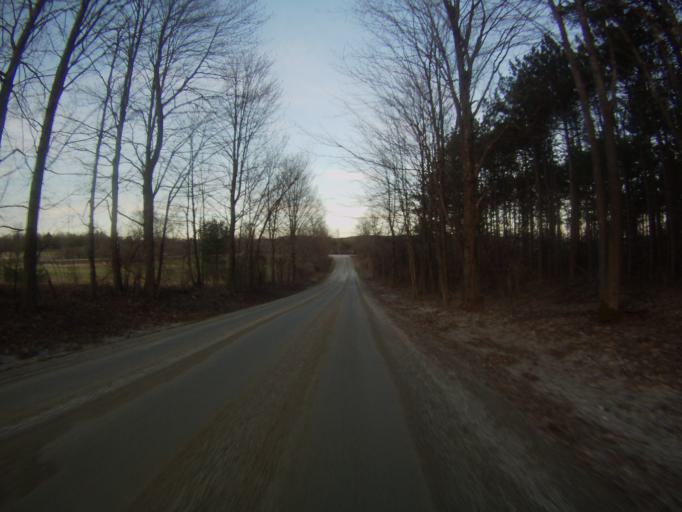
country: US
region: Vermont
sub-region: Addison County
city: Middlebury (village)
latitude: 44.0252
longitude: -73.1965
